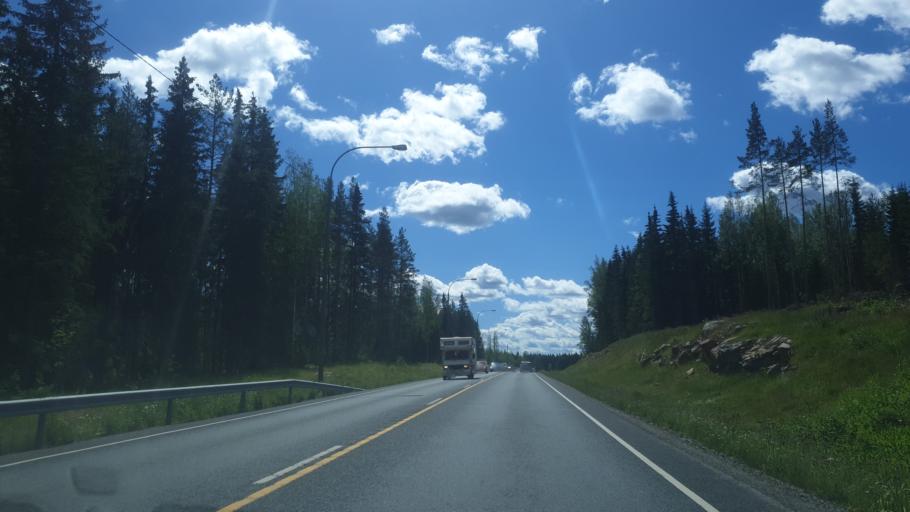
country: FI
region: Northern Savo
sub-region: Varkaus
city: Leppaevirta
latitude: 62.6128
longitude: 27.6231
